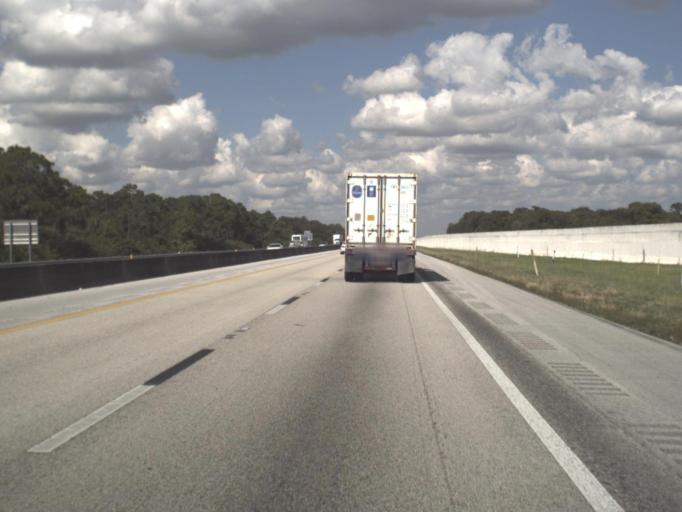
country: US
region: Florida
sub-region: Palm Beach County
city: Limestone Creek
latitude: 26.9500
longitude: -80.1623
